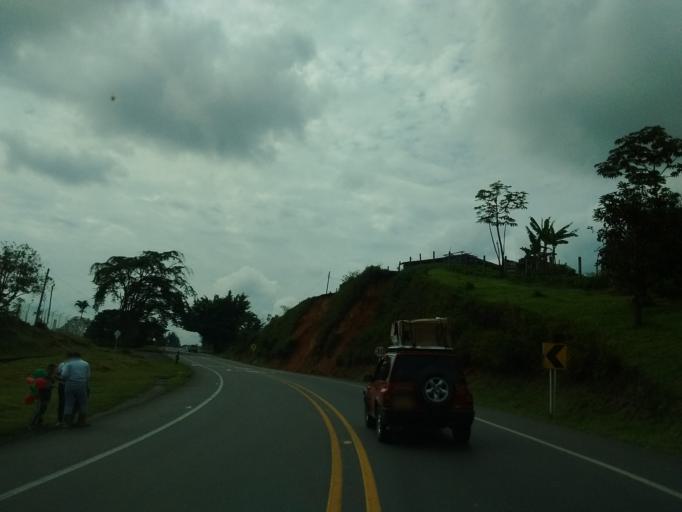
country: CO
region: Cauca
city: Morales
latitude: 2.7831
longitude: -76.5556
